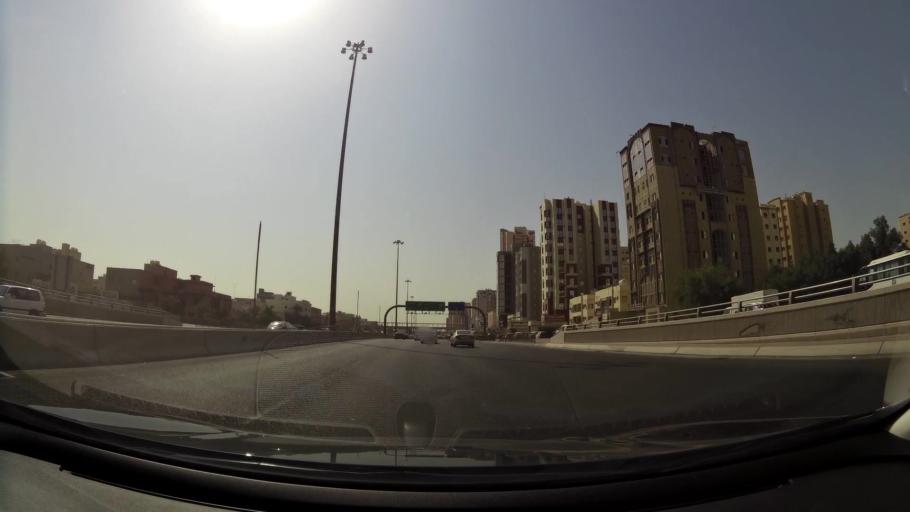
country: KW
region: Muhafazat Hawalli
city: Ar Rumaythiyah
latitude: 29.3224
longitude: 48.0643
